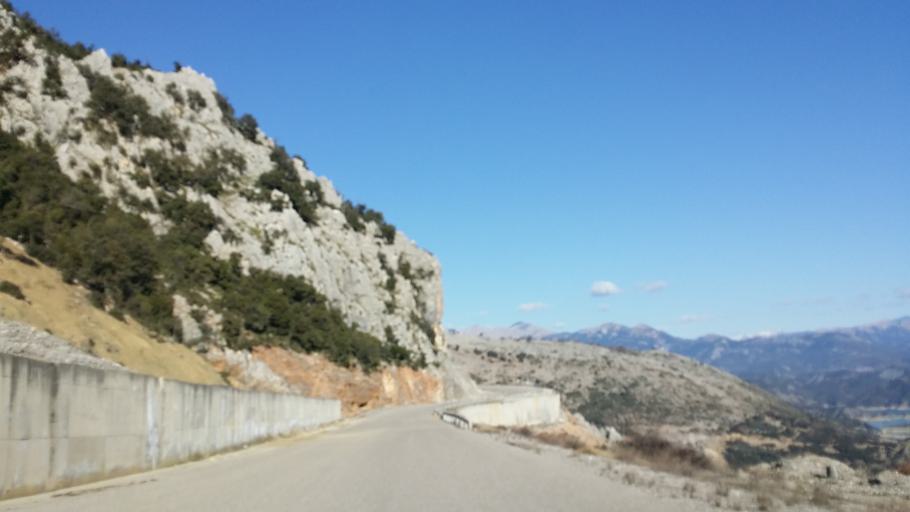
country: GR
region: Central Greece
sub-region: Nomos Evrytanias
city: Kerasochori
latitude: 38.9523
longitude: 21.4662
